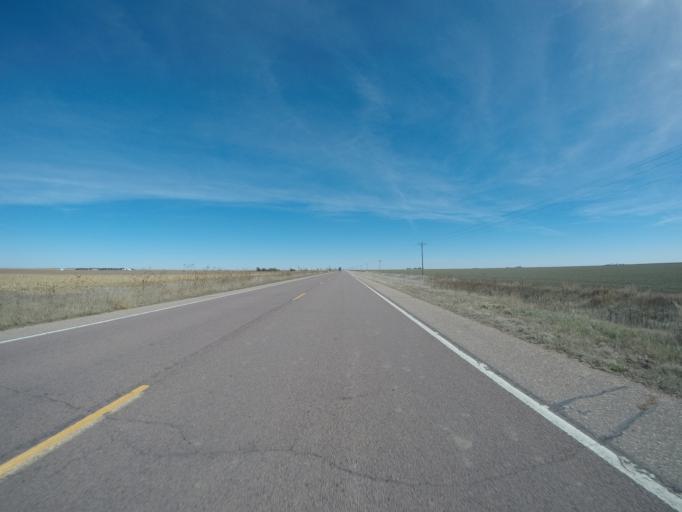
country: US
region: Colorado
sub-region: Kit Carson County
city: Burlington
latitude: 39.6577
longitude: -102.4610
